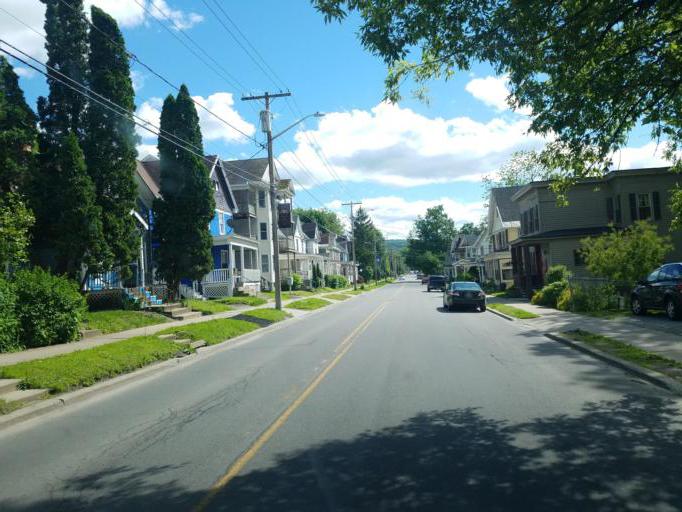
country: US
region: New York
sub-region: Herkimer County
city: Ilion
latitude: 43.0115
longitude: -75.0389
